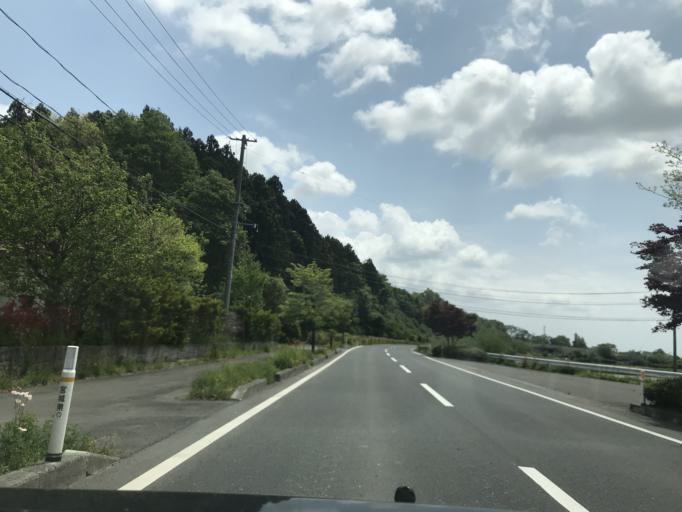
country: JP
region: Miyagi
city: Furukawa
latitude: 38.6673
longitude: 141.0000
